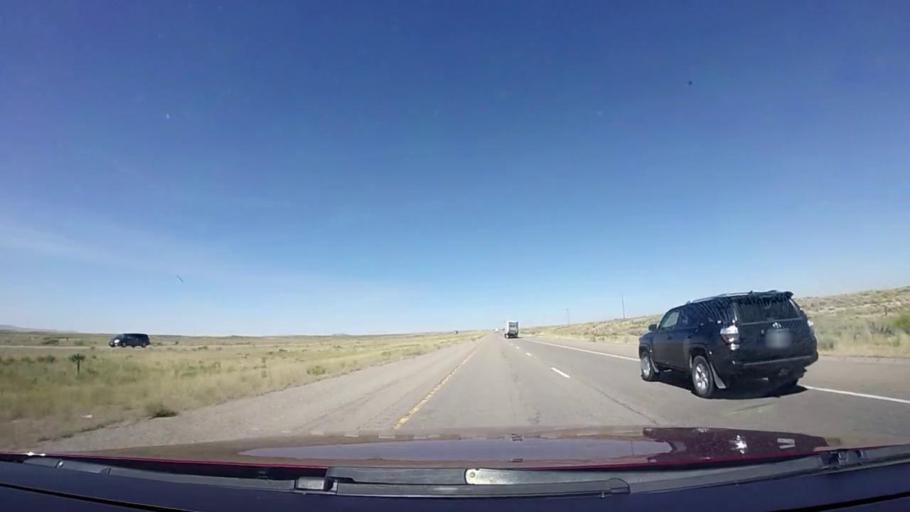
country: US
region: Wyoming
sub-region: Sweetwater County
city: Rock Springs
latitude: 41.6375
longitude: -108.4420
